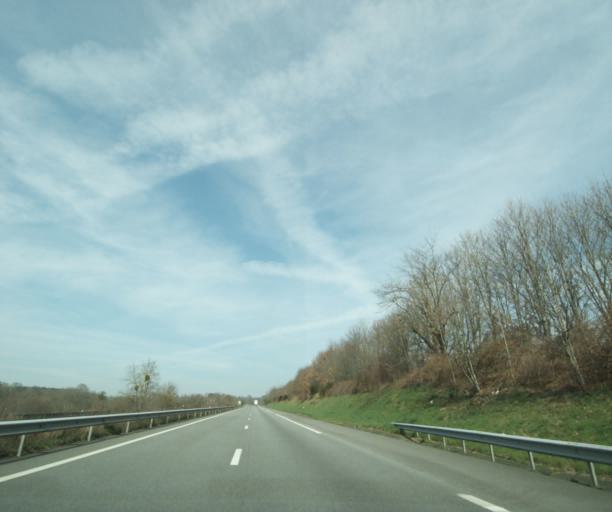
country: FR
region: Limousin
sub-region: Departement de la Correze
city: Vigeois
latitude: 45.4232
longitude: 1.5162
